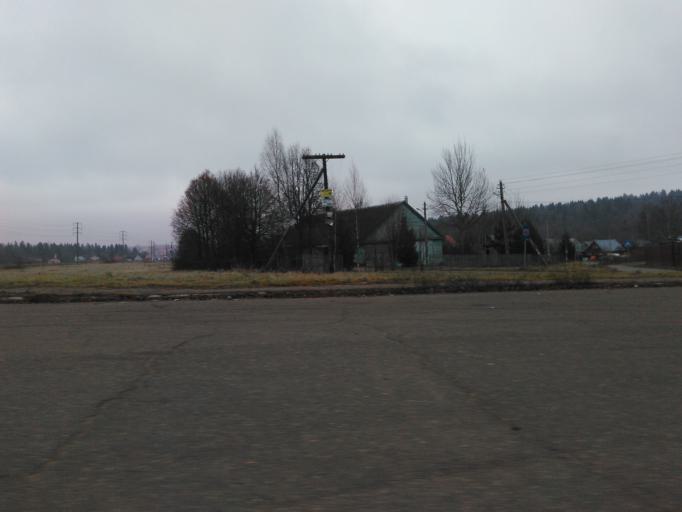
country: RU
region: Moskovskaya
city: Muranovo
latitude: 56.1790
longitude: 37.9049
